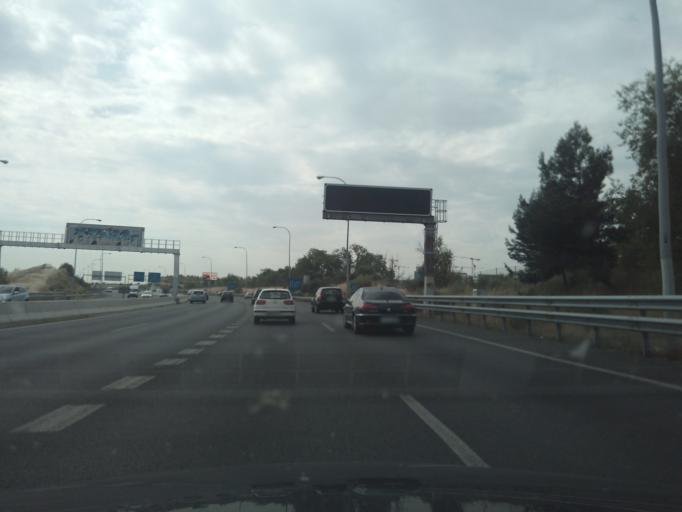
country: ES
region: Madrid
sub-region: Provincia de Madrid
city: San Blas
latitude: 40.4476
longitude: -3.6032
